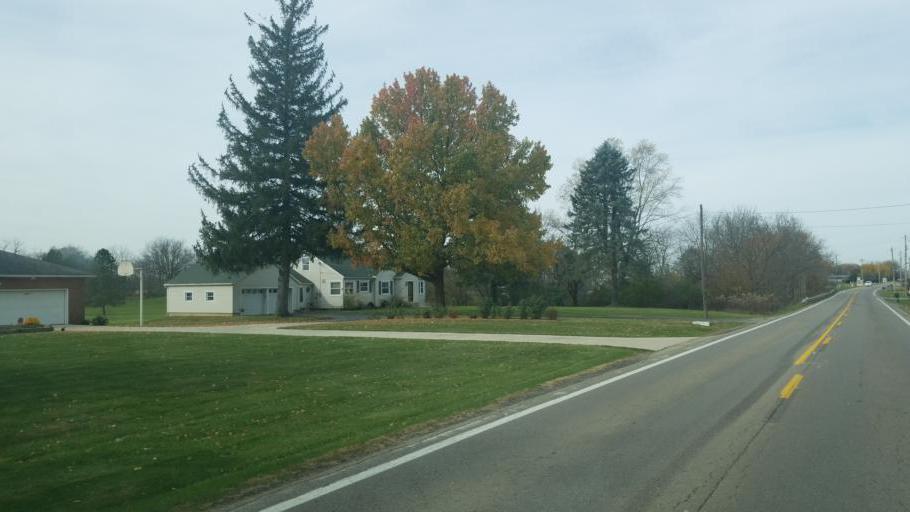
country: US
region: Ohio
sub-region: Madison County
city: London
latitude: 39.8993
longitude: -83.4642
